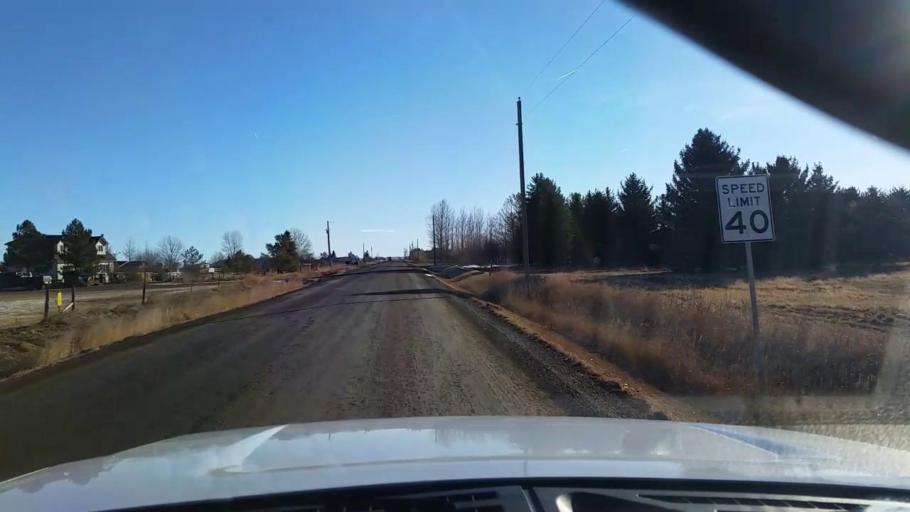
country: US
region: Colorado
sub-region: Larimer County
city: Wellington
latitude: 40.7696
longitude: -105.0859
